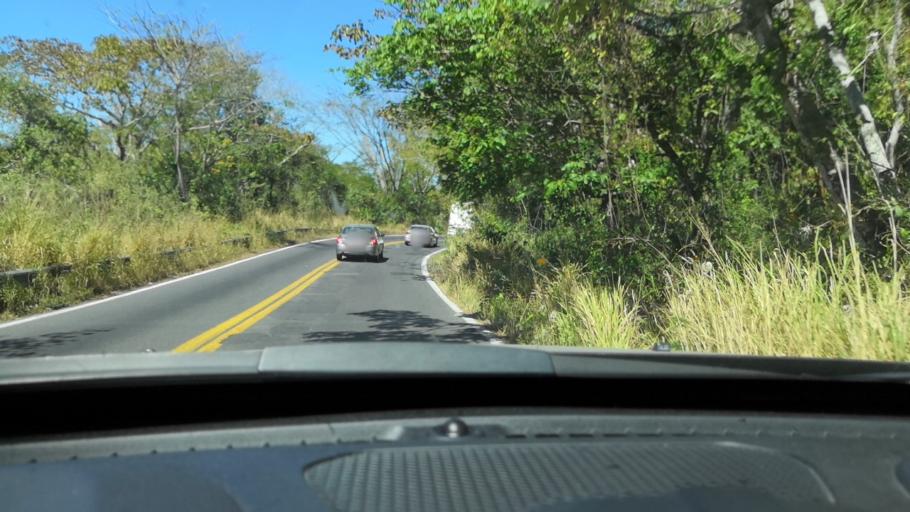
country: MX
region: Nayarit
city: Compostela
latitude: 21.2184
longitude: -104.9964
